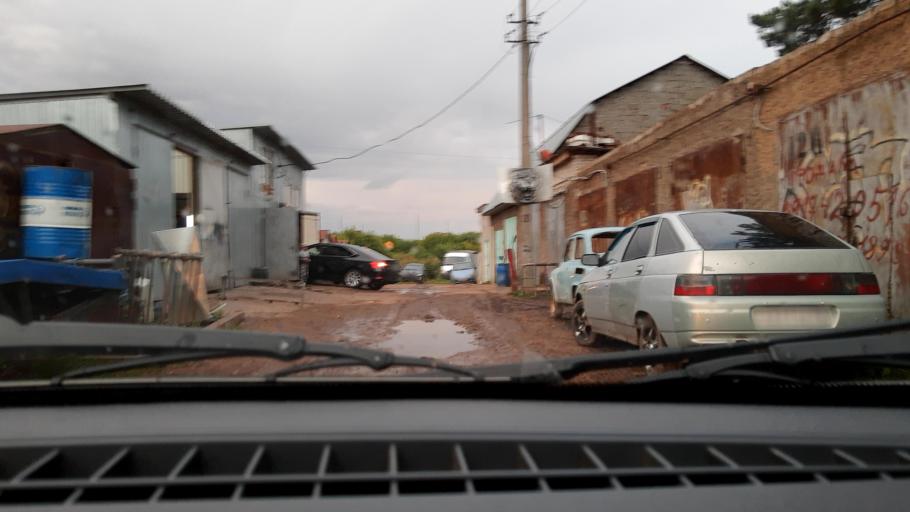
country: RU
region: Bashkortostan
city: Mikhaylovka
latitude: 54.7875
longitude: 55.8716
